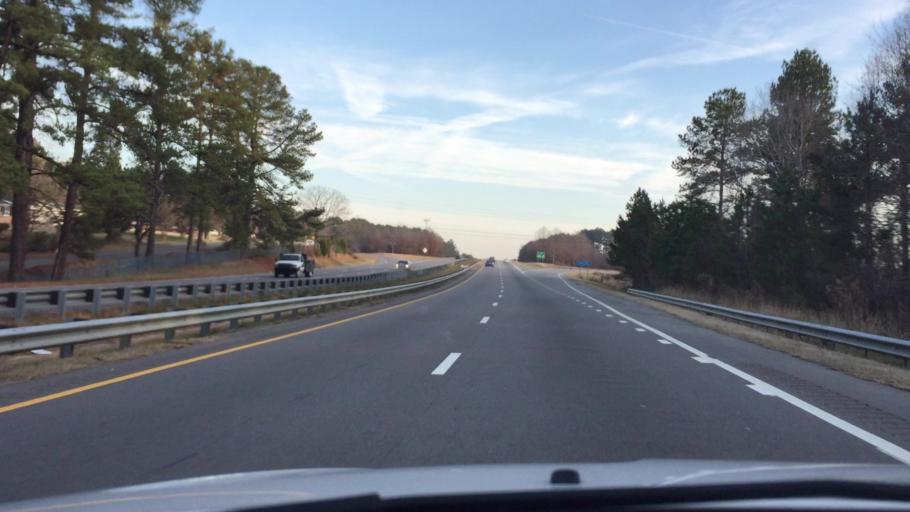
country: US
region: North Carolina
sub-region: Lee County
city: Sanford
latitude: 35.4644
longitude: -79.2044
